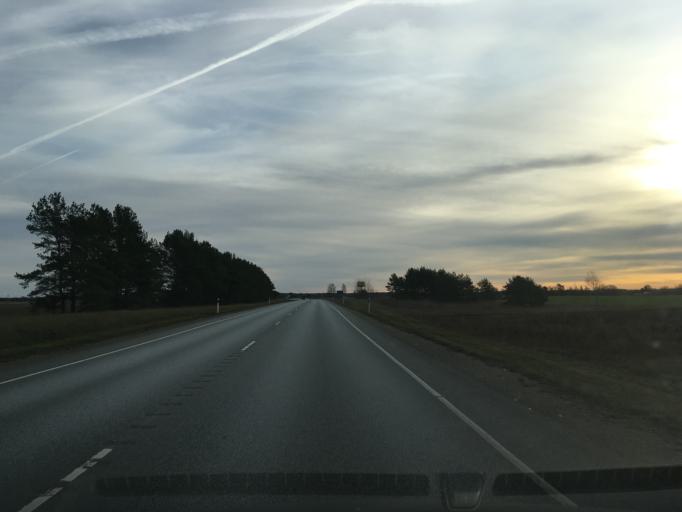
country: EE
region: Ida-Virumaa
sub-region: Puessi linn
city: Pussi
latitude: 59.4054
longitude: 27.0634
